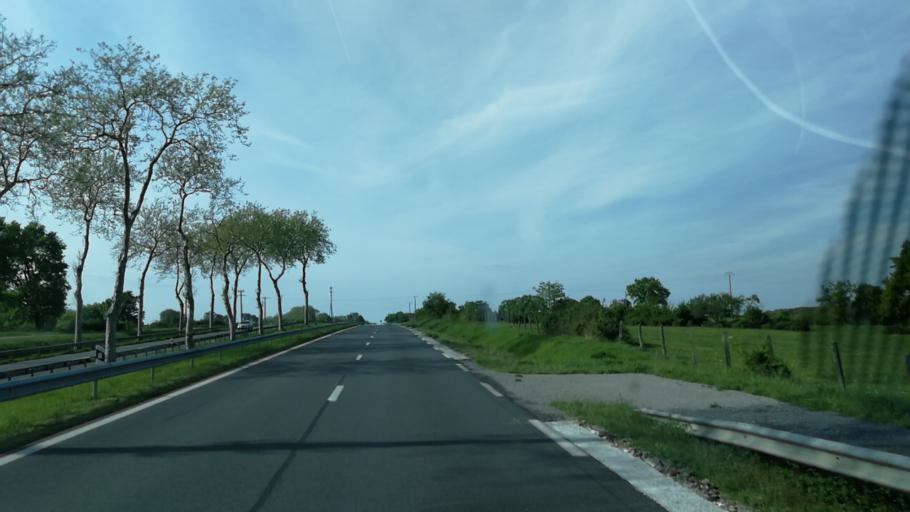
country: FR
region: Bourgogne
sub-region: Departement de la Nievre
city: Saint-Pierre-le-Moutier
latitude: 46.7727
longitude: 3.1331
